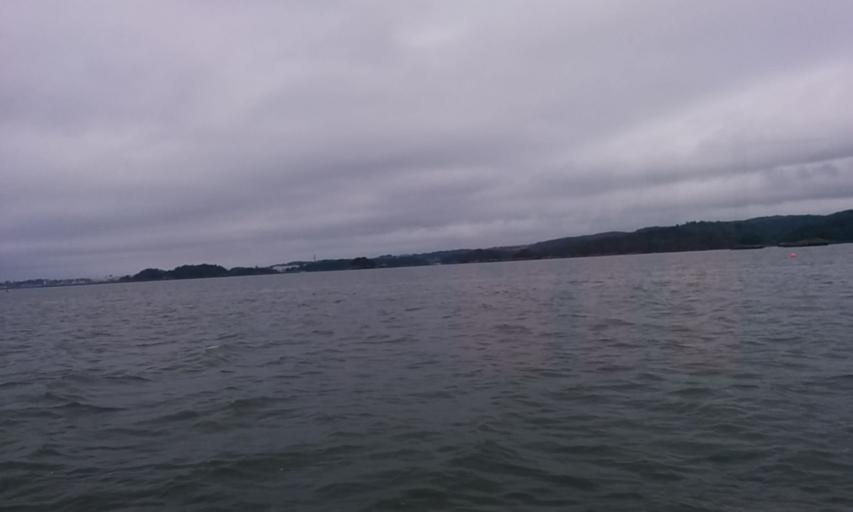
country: JP
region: Miyagi
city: Matsushima
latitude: 38.3498
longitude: 141.0749
